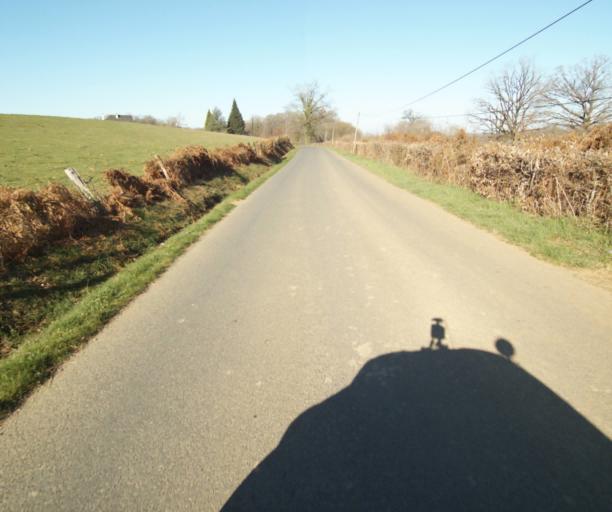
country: FR
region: Limousin
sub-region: Departement de la Correze
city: Saint-Clement
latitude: 45.3665
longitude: 1.6493
